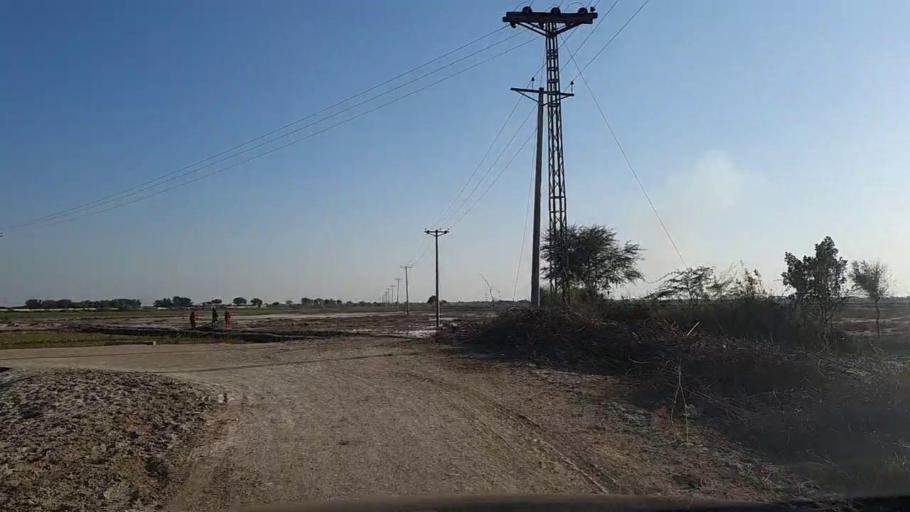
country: PK
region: Sindh
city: Nawabshah
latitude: 26.2012
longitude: 68.3753
